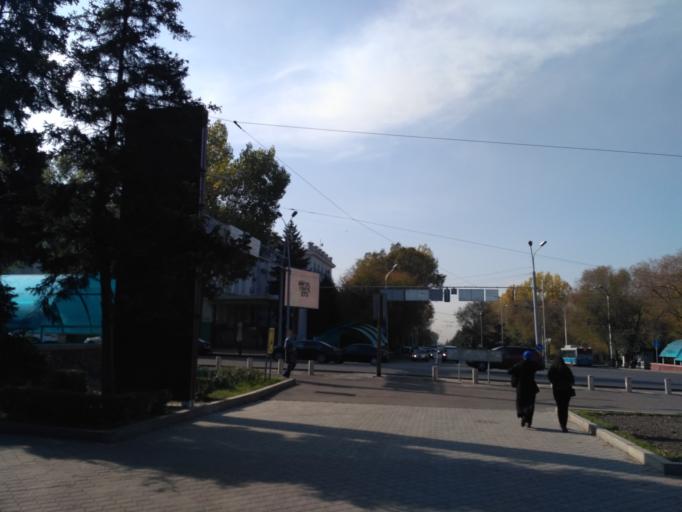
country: KZ
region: Almaty Qalasy
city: Almaty
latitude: 43.2430
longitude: 76.9575
